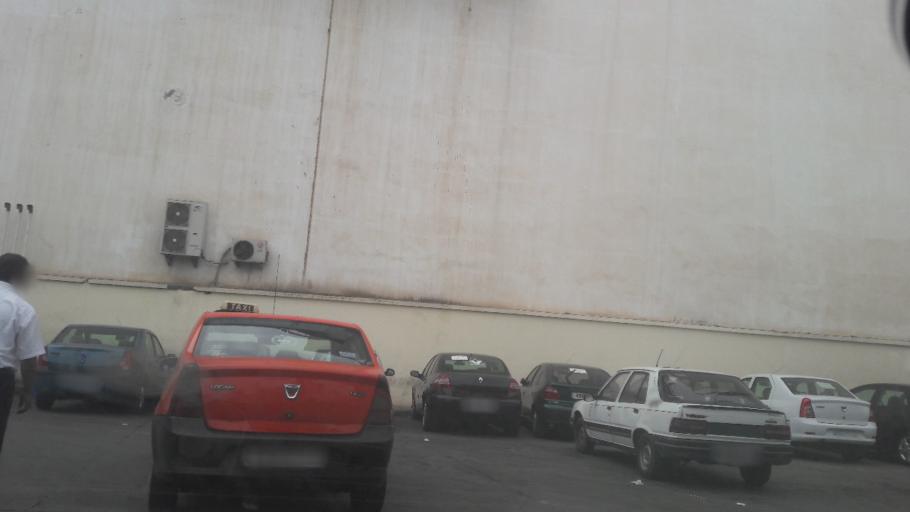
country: MA
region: Souss-Massa-Draa
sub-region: Agadir-Ida-ou-Tnan
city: Agadir
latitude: 30.4121
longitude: -9.5911
